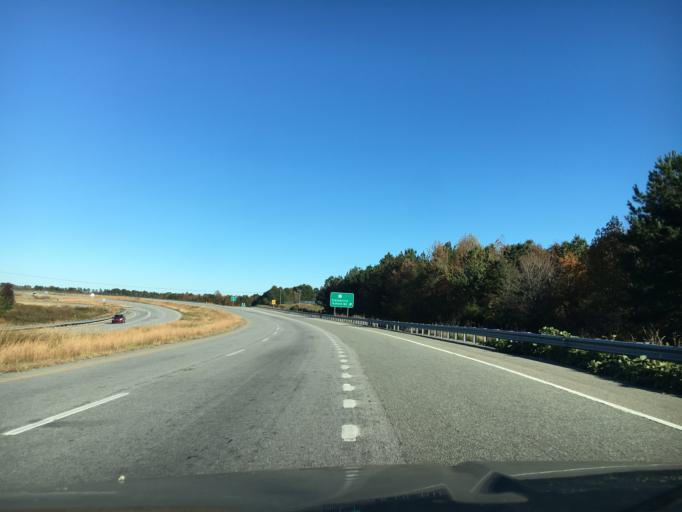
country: US
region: Virginia
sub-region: Mecklenburg County
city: Clarksville
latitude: 36.6052
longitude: -78.5707
